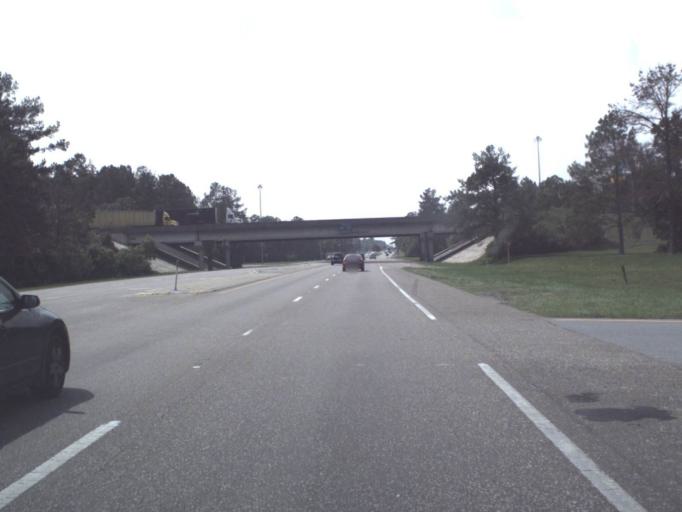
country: US
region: Florida
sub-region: Nassau County
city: Nassau Village-Ratliff
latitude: 30.4137
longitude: -81.7485
